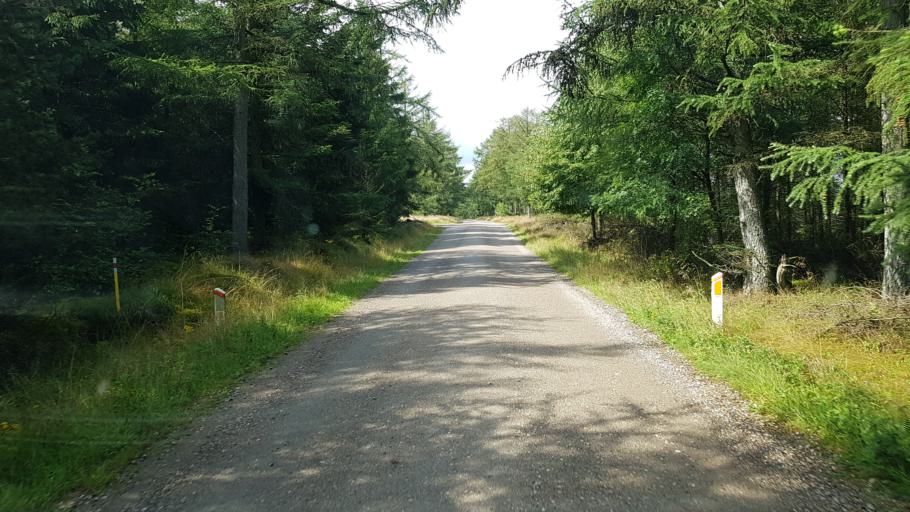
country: DK
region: South Denmark
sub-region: Vejen Kommune
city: Holsted
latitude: 55.5947
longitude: 8.9078
